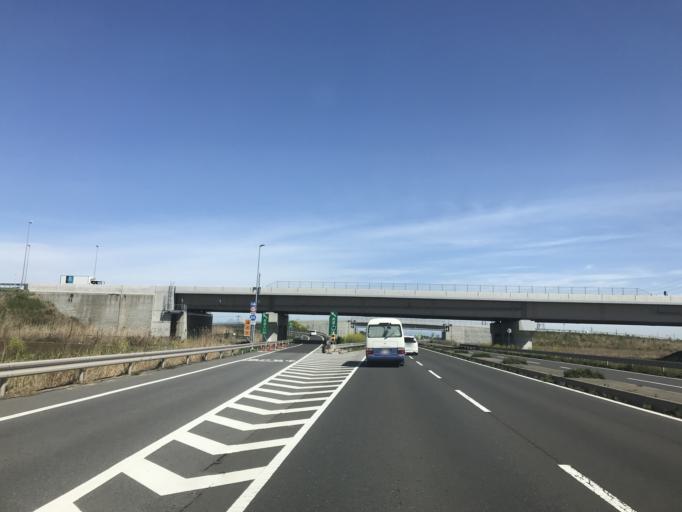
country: JP
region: Ibaraki
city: Ishige
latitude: 36.0776
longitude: 139.9863
